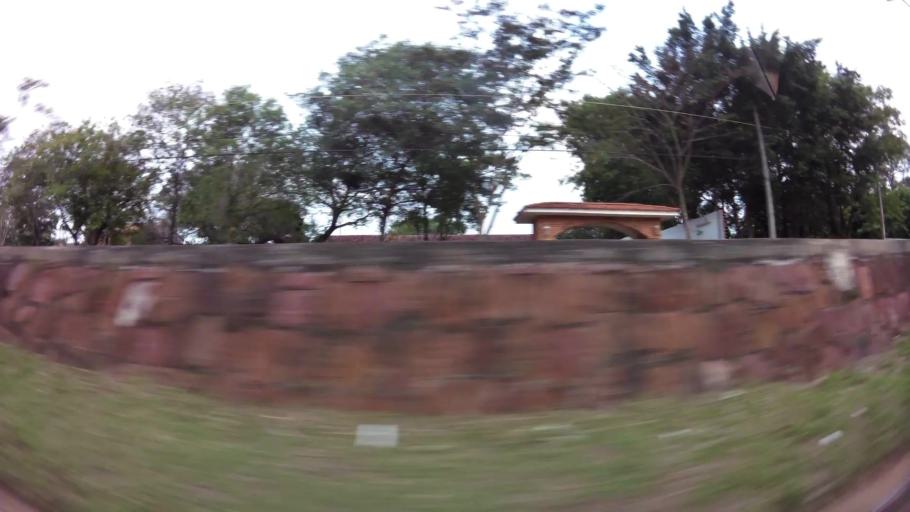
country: PY
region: Central
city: Lambare
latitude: -25.3452
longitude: -57.6388
